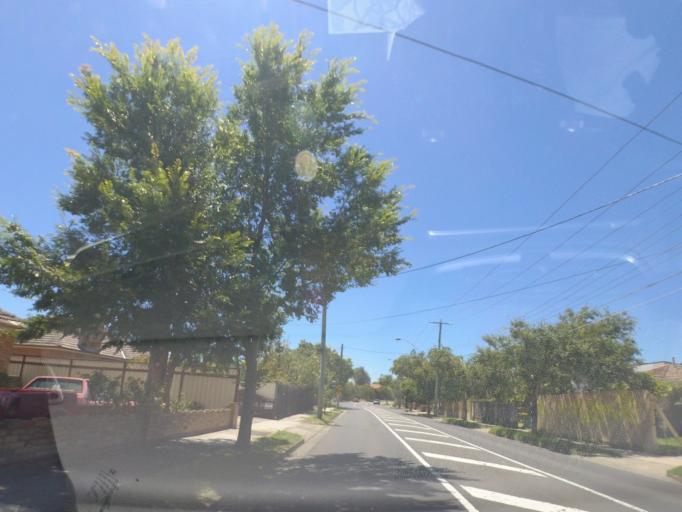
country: AU
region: Victoria
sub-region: Darebin
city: Reservoir
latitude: -37.7238
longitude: 145.0017
